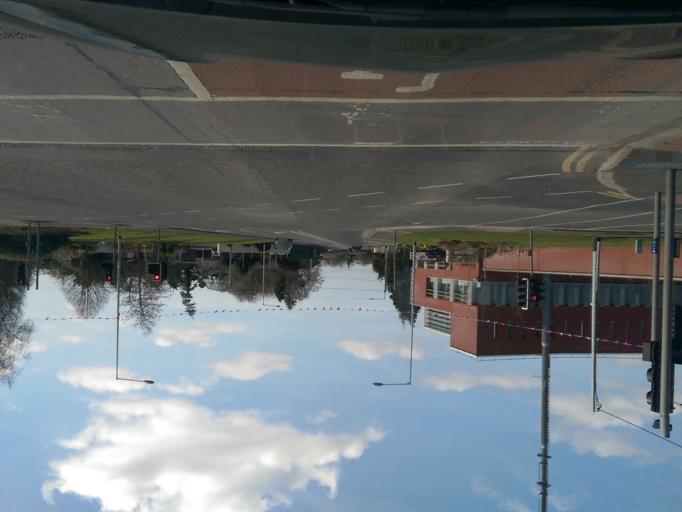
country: IE
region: Leinster
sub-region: Kildare
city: Leixlip
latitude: 53.3676
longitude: -6.4995
